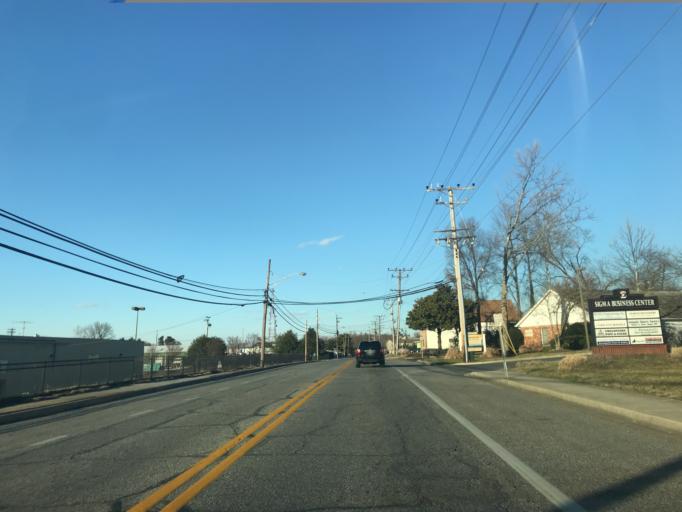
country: US
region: Maryland
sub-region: Anne Arundel County
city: Parole
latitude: 38.9792
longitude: -76.5361
